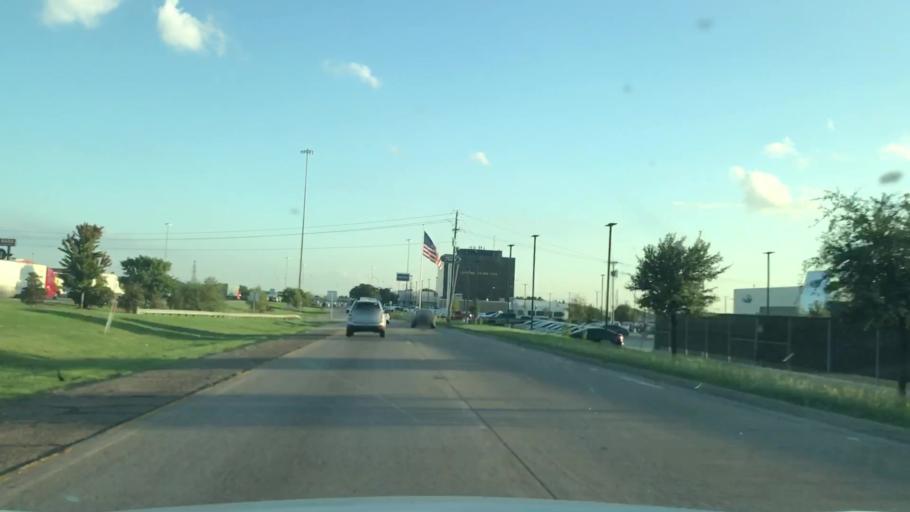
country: US
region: Texas
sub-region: Dallas County
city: Mesquite
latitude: 32.8076
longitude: -96.6279
